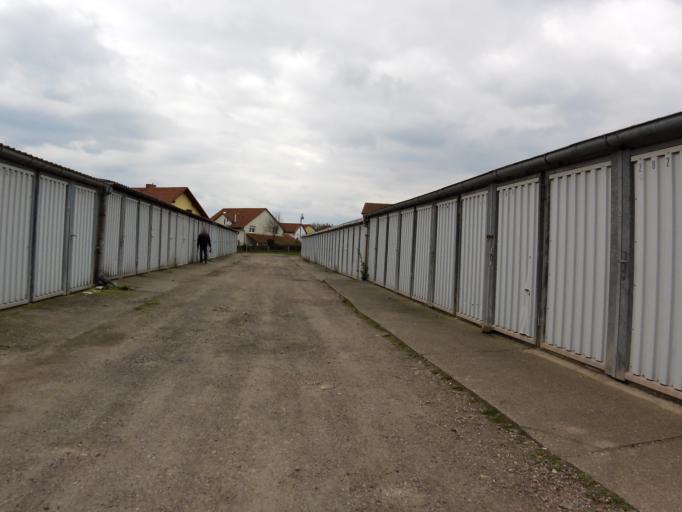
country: DE
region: Thuringia
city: Gotha
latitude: 50.9499
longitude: 10.6749
